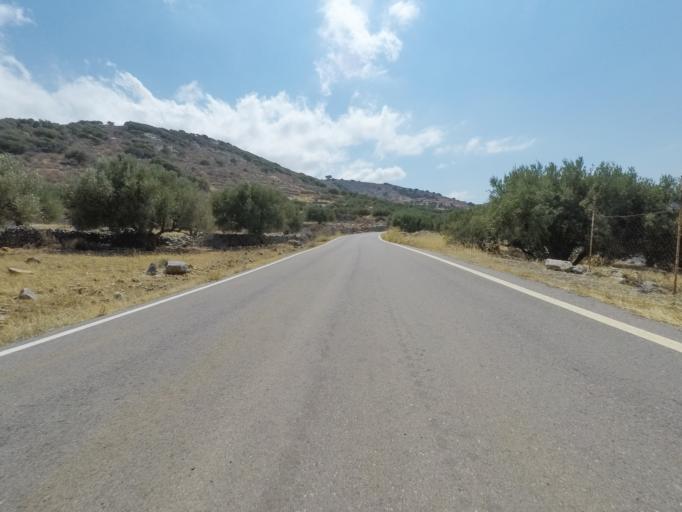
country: GR
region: Crete
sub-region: Nomos Lasithiou
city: Elounda
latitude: 35.3178
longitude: 25.6883
